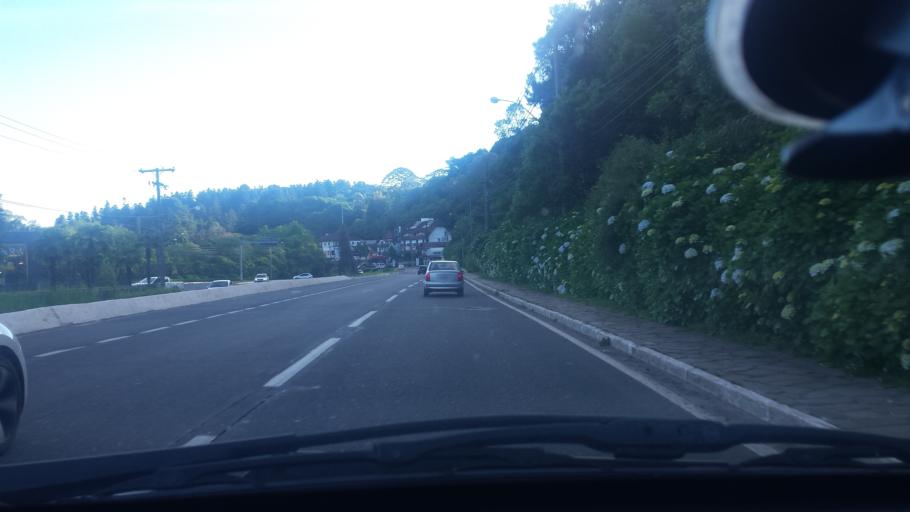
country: BR
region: Rio Grande do Sul
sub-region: Canela
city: Canela
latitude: -29.3713
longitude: -50.8633
